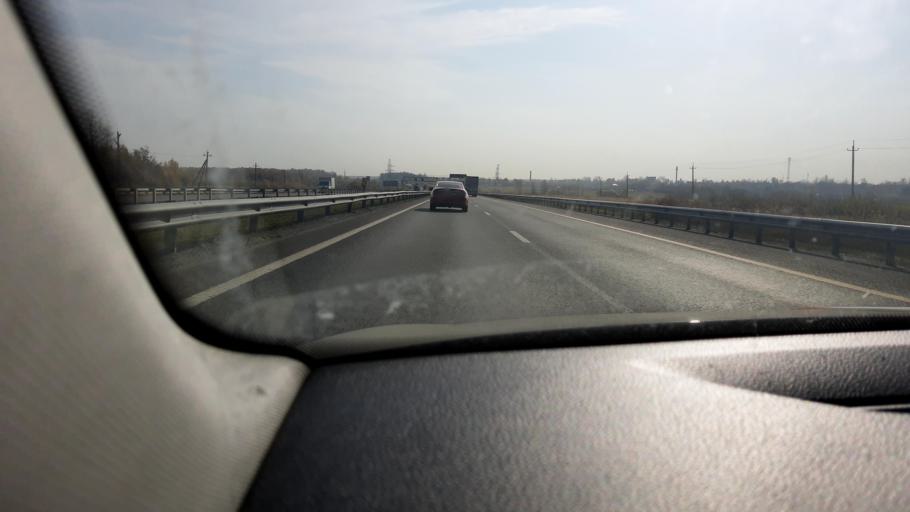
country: RU
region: Moskovskaya
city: Zhilevo
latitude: 54.9858
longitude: 37.9609
